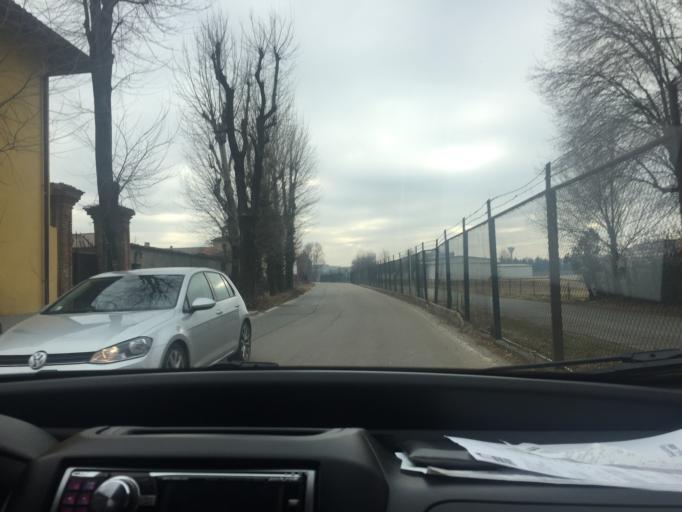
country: IT
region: Piedmont
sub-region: Provincia di Torino
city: Savonera
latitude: 45.0859
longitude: 7.6111
